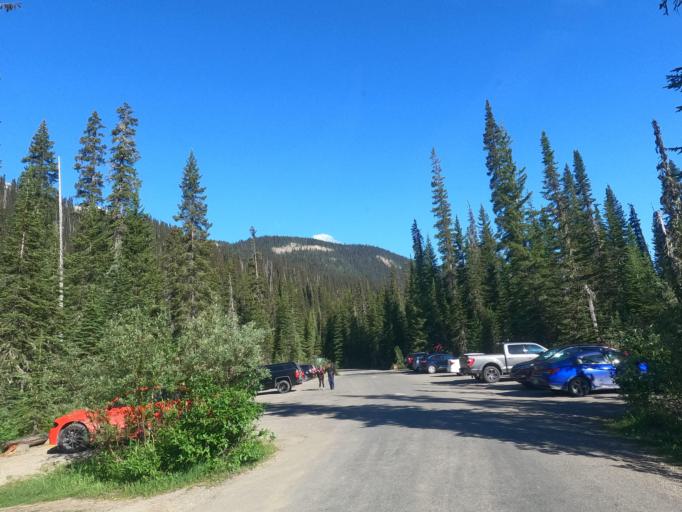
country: CA
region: Alberta
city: Lake Louise
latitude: 51.4980
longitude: -116.4835
